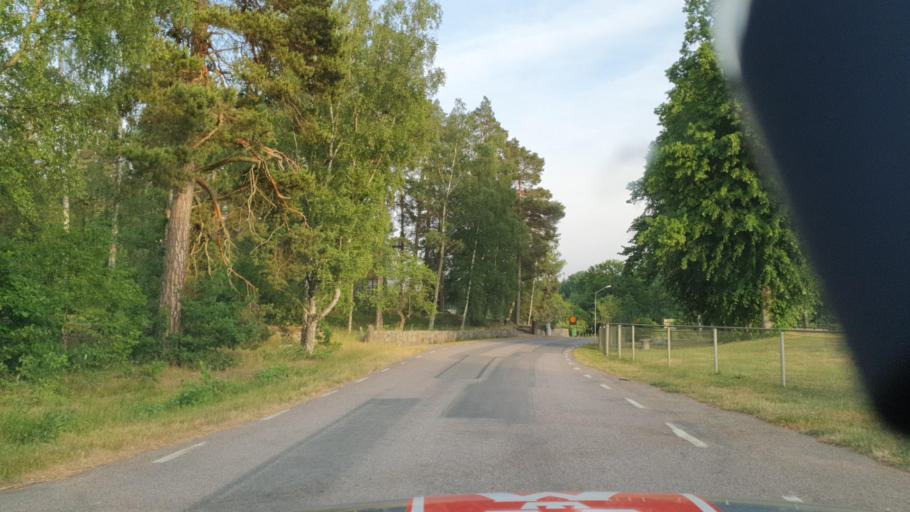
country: SE
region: Kalmar
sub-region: Torsas Kommun
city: Torsas
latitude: 56.4974
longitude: 16.1024
